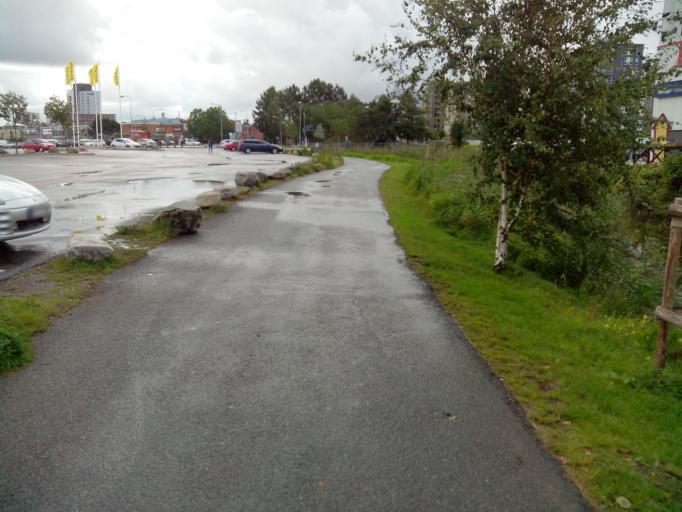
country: SE
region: Vaestra Goetaland
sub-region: Goteborg
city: Goeteborg
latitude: 57.7253
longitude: 11.9511
